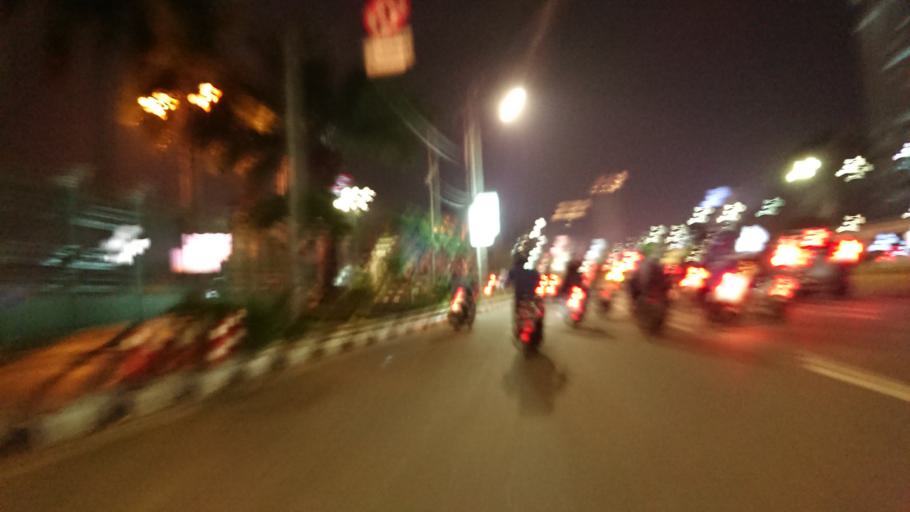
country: ID
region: Jakarta Raya
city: Jakarta
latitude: -6.2084
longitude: 106.8036
